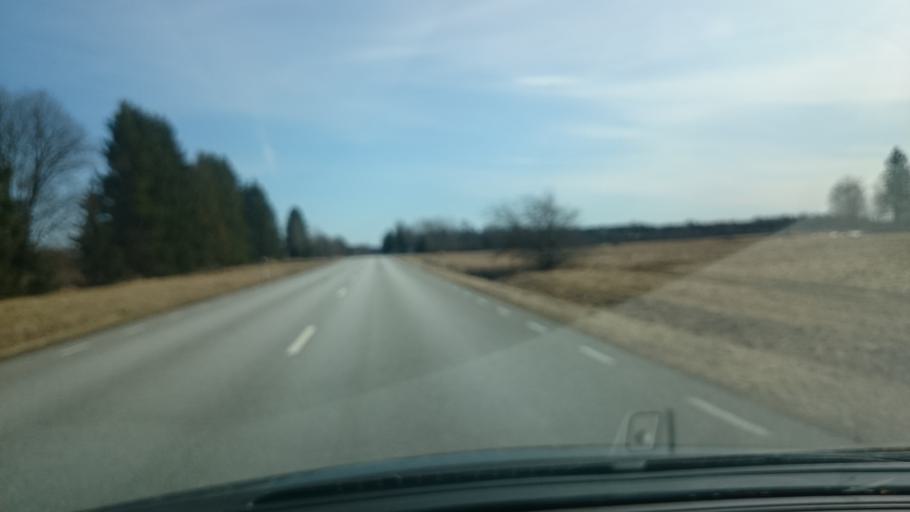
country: EE
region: Paernumaa
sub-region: Tootsi vald
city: Tootsi
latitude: 58.6543
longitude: 24.8432
